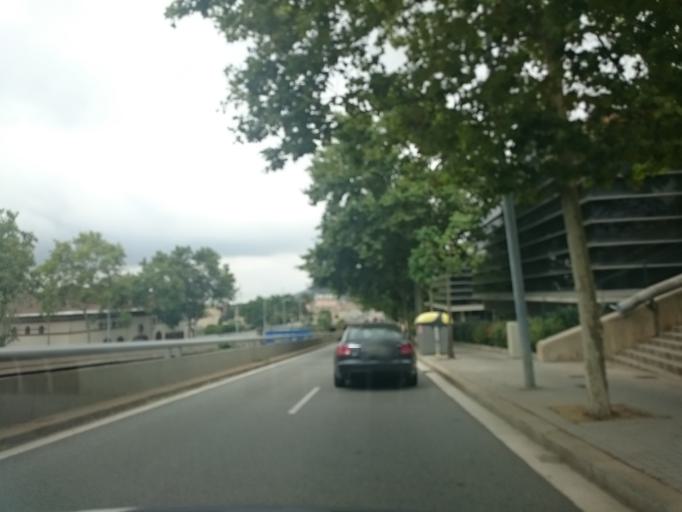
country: ES
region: Catalonia
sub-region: Provincia de Barcelona
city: Sarria-Sant Gervasi
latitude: 41.4072
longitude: 2.1218
